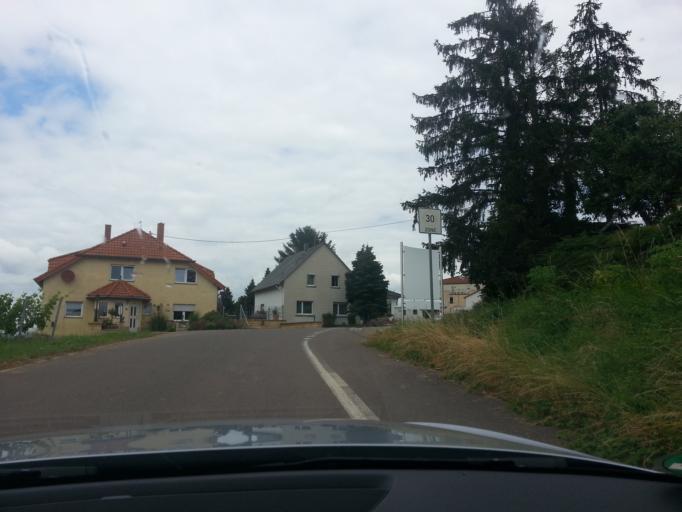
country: DE
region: Saarland
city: Perl
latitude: 49.4668
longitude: 6.3770
